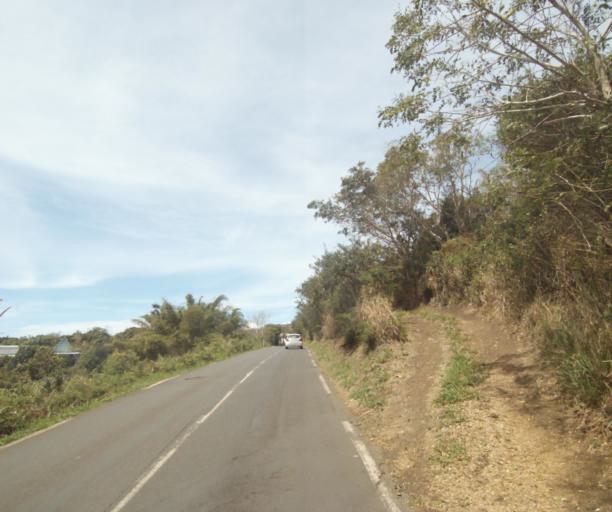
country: RE
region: Reunion
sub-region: Reunion
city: Saint-Paul
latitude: -21.0485
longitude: 55.2770
